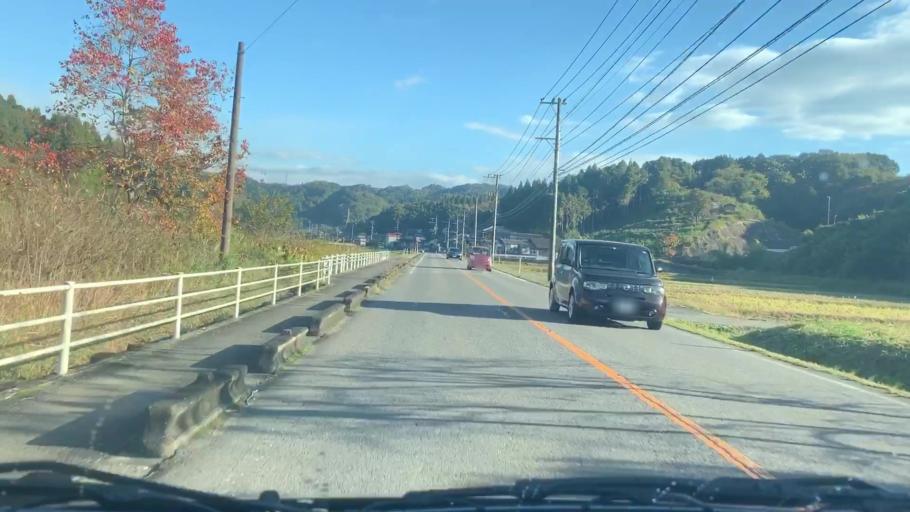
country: JP
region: Saga Prefecture
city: Takeocho-takeo
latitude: 33.2271
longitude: 130.0579
